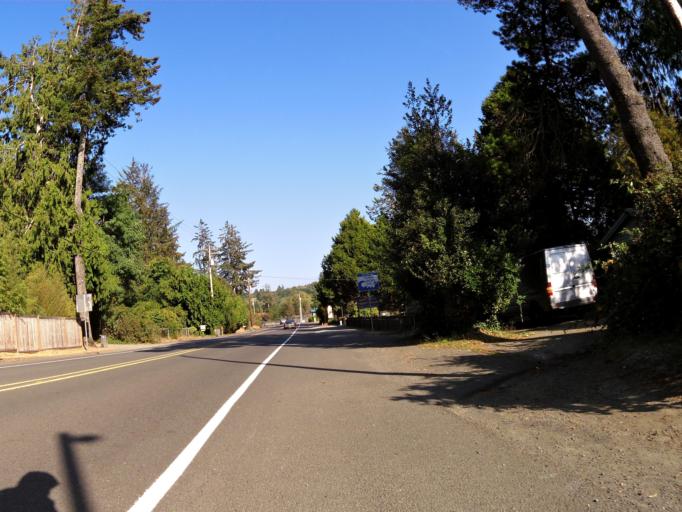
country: US
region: Oregon
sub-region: Tillamook County
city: Rockaway Beach
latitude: 45.7173
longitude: -123.9132
